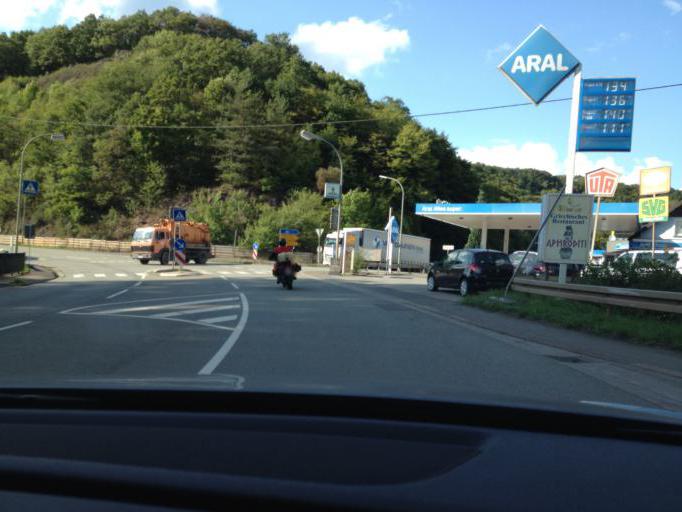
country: DE
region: Saarland
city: Schmelz
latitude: 49.4626
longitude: 6.8521
